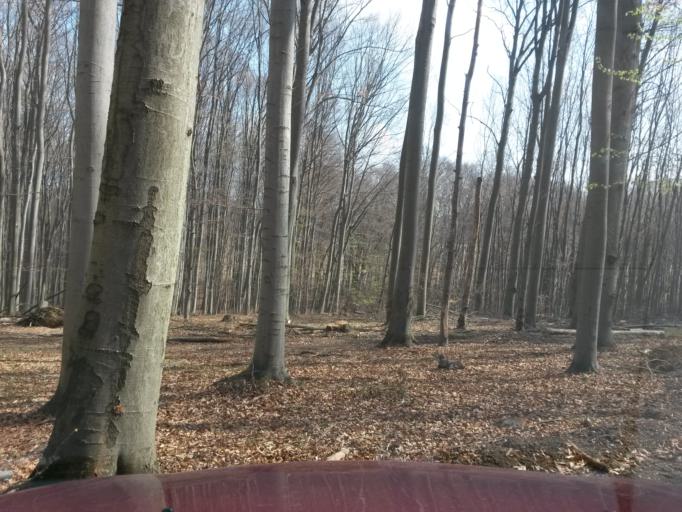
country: SK
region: Presovsky
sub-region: Okres Presov
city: Presov
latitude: 48.9337
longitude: 21.1395
